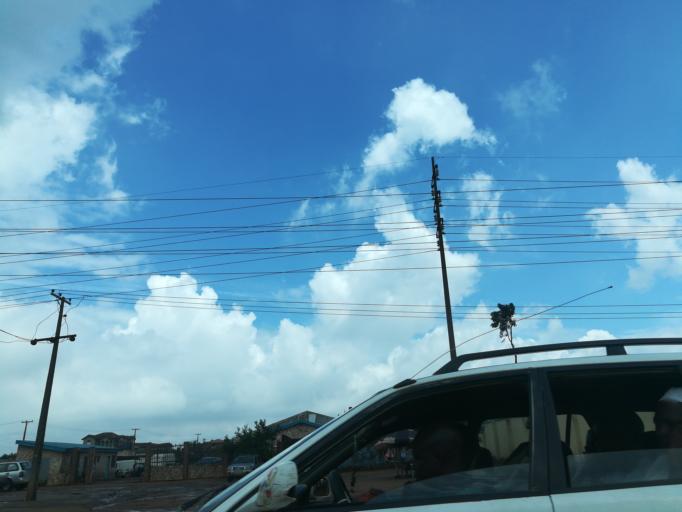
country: NG
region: Lagos
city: Ikorodu
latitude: 6.6590
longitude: 3.5195
